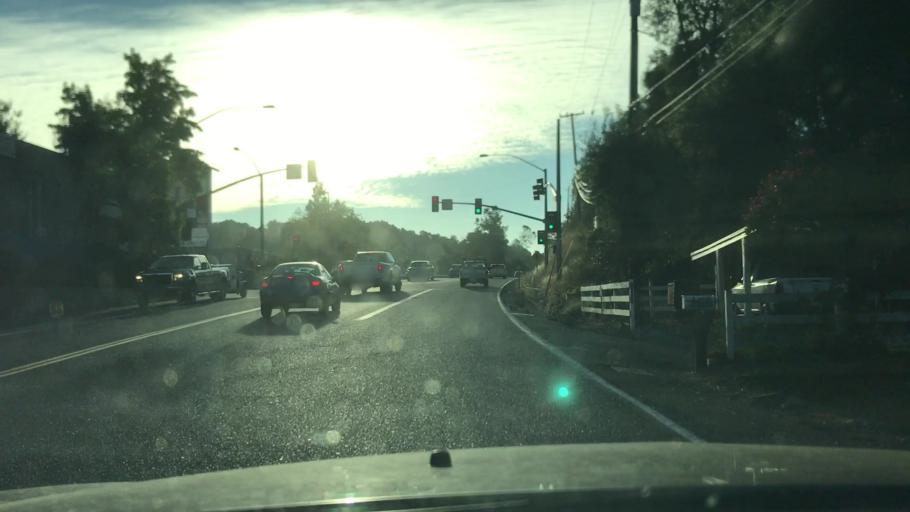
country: US
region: California
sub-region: Tuolumne County
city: East Sonora
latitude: 37.9740
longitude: -120.3444
